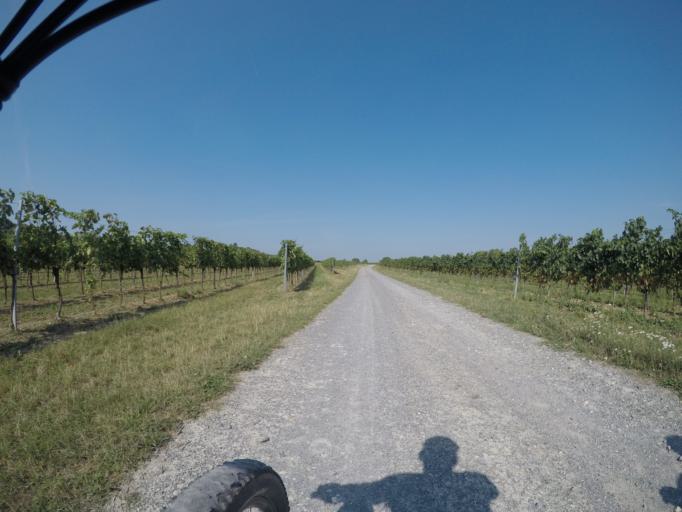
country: AT
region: Lower Austria
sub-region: Politischer Bezirk Baden
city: Hirtenberg
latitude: 47.9514
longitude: 16.1771
